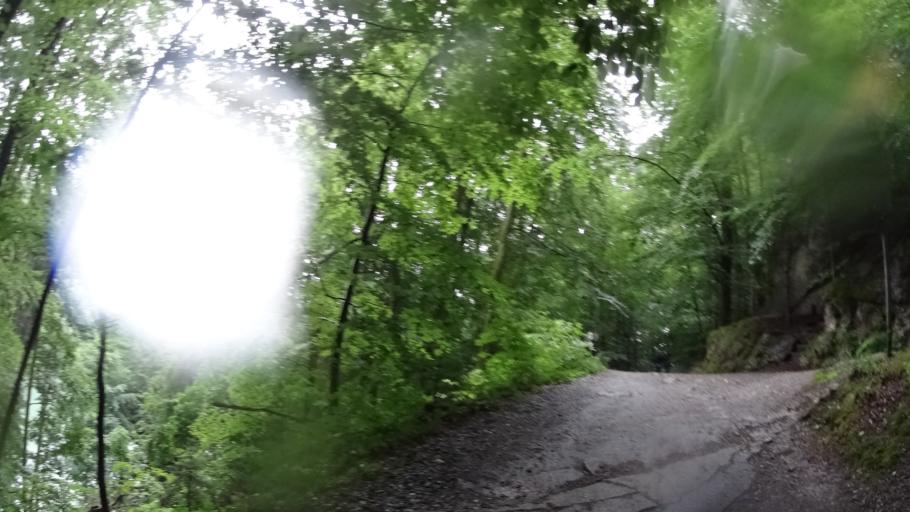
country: AT
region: Upper Austria
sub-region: Politischer Bezirk Scharding
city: Scharding
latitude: 48.4945
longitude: 13.4460
